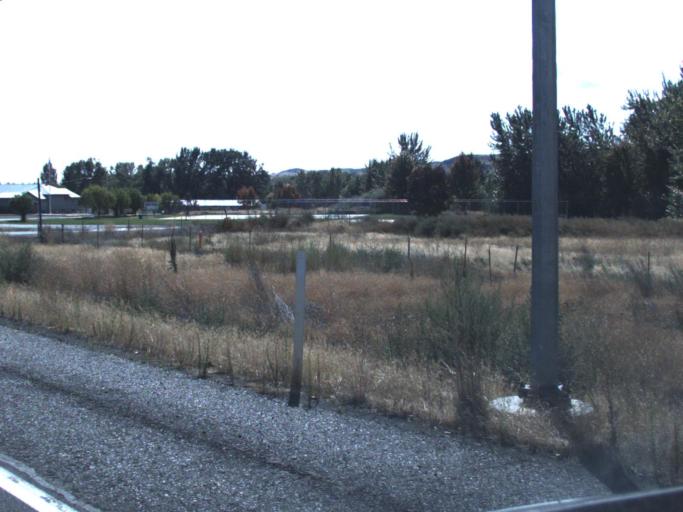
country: US
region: Washington
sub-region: Yakima County
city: Tieton
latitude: 46.7182
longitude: -120.6795
